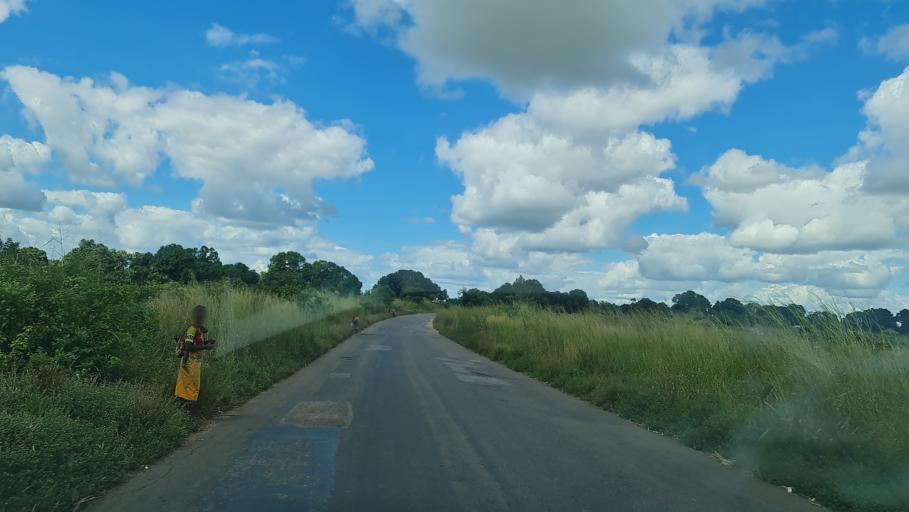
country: MZ
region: Zambezia
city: Quelimane
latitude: -17.5136
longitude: 36.2583
